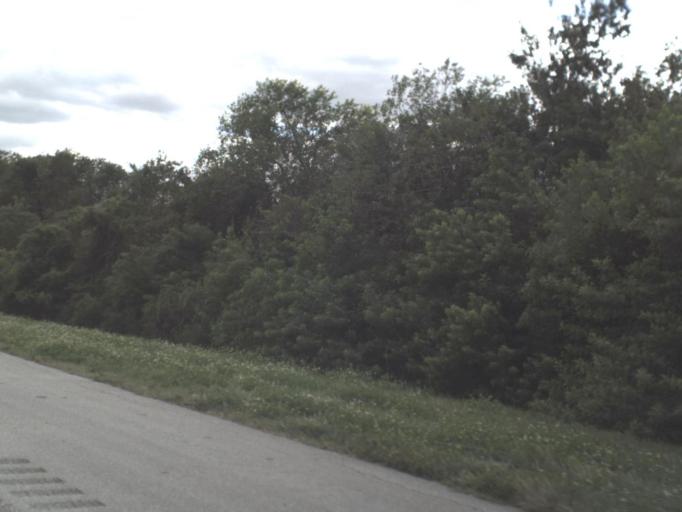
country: US
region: Florida
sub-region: Osceola County
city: Buenaventura Lakes
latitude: 28.2942
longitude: -81.3537
